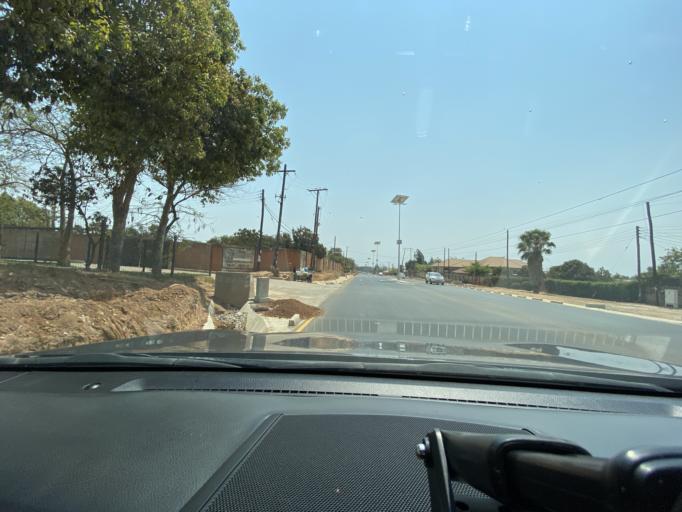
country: ZM
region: Lusaka
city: Lusaka
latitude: -15.3710
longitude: 28.3458
